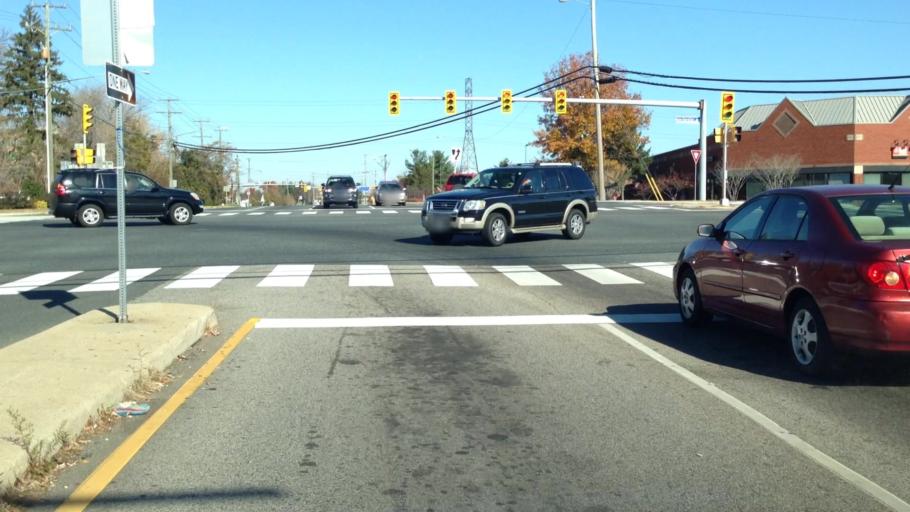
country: US
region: Virginia
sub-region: Fairfax County
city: Franconia
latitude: 38.7652
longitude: -77.1558
